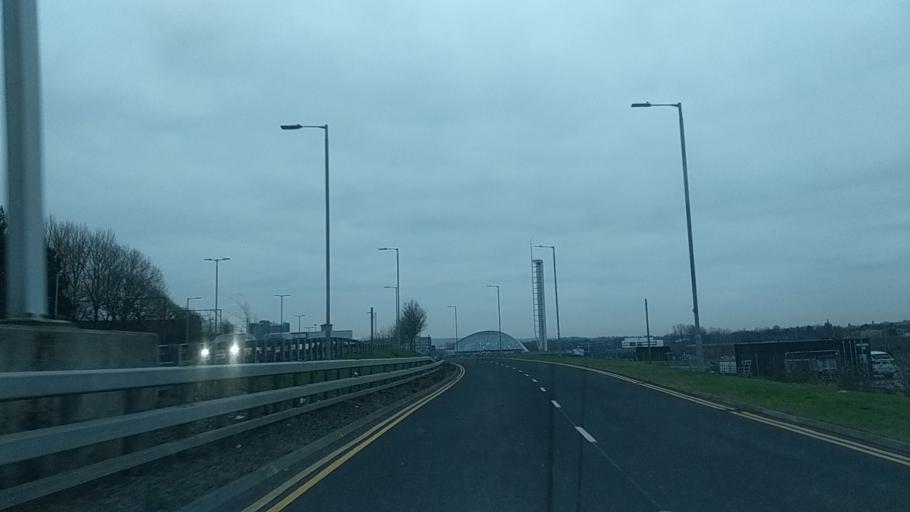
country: GB
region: Scotland
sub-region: Glasgow City
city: Glasgow
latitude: 55.8655
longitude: -4.3024
